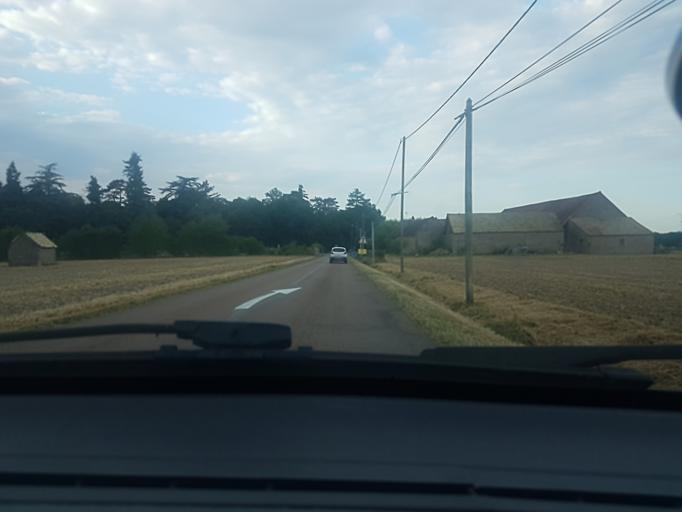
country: FR
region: Bourgogne
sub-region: Departement de Saone-et-Loire
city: Buxy
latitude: 46.7068
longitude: 4.7730
